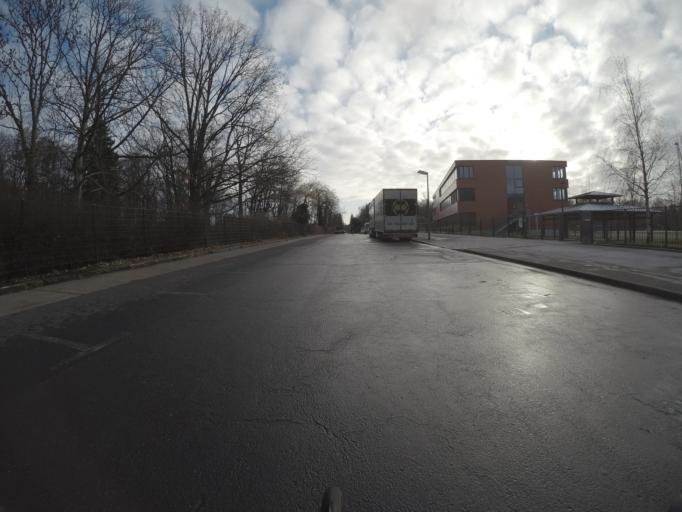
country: DE
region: Berlin
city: Weissensee
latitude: 52.5587
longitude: 13.4507
